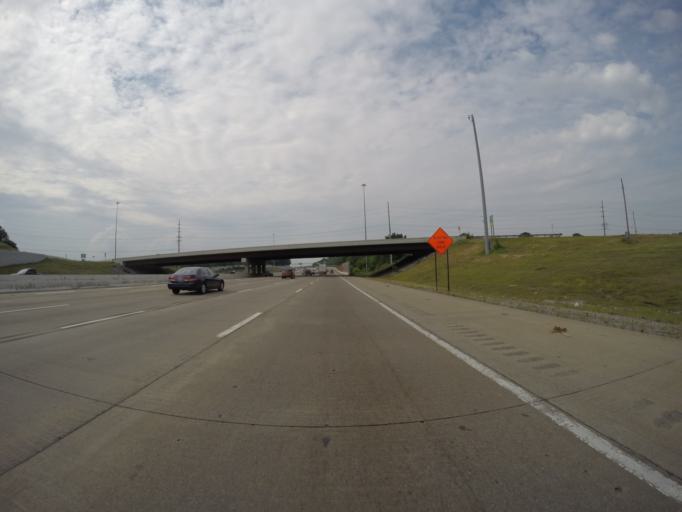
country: US
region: Tennessee
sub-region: Davidson County
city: Goodlettsville
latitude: 36.2657
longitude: -86.7376
